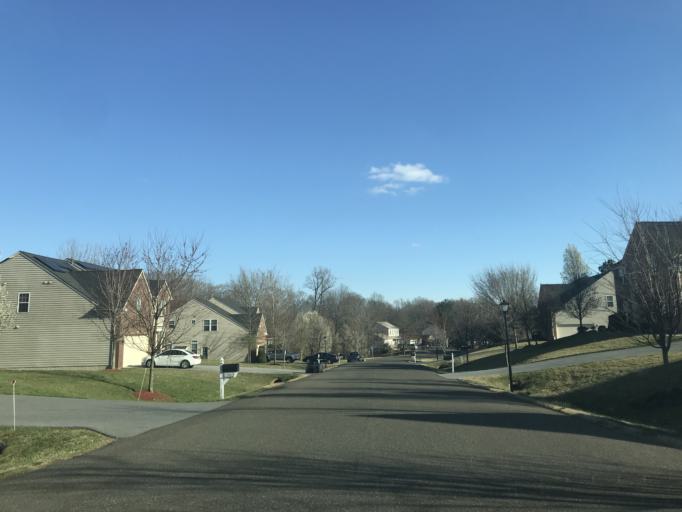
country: US
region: Maryland
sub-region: Prince George's County
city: Woodmore
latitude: 38.9107
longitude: -76.7929
